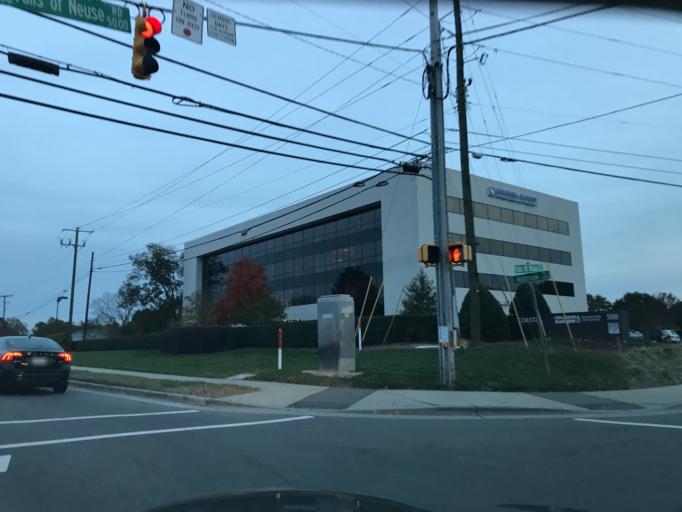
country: US
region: North Carolina
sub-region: Wake County
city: West Raleigh
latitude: 35.8506
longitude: -78.6144
